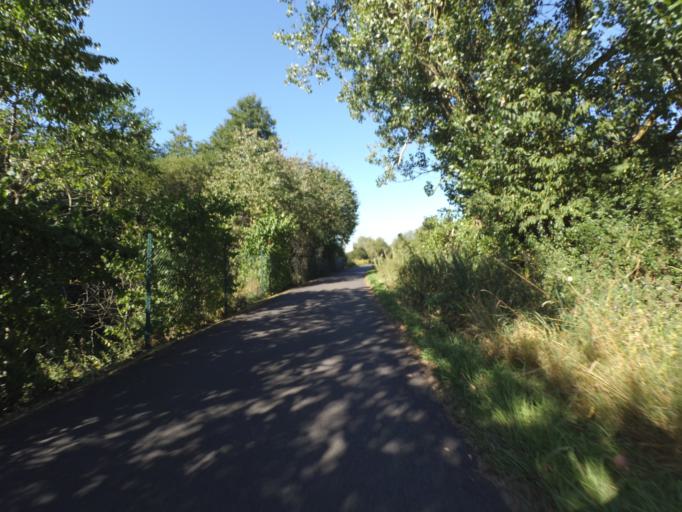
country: DE
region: Rheinland-Pfalz
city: Udler
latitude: 50.1546
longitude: 6.8770
